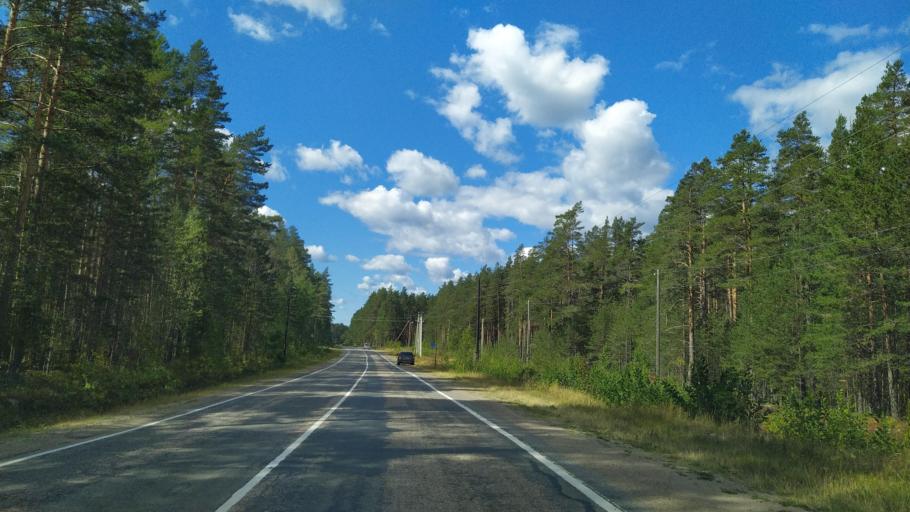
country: RU
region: Leningrad
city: Priozersk
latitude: 61.0047
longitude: 30.2183
